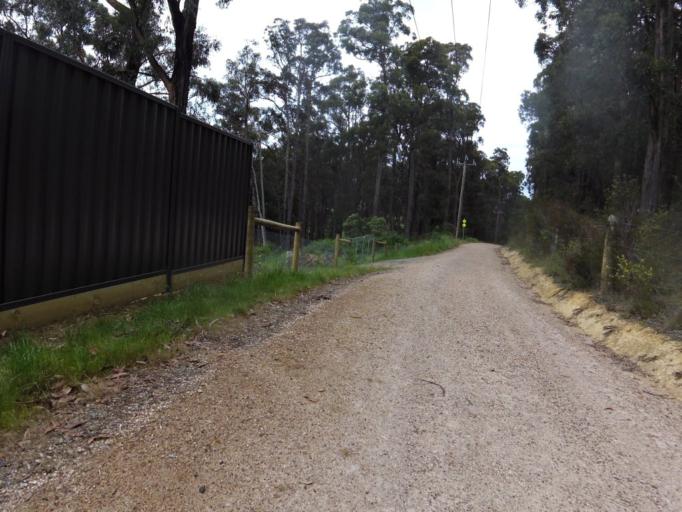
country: AU
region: Victoria
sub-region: Cardinia
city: Cockatoo
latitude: -37.9436
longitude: 145.5021
